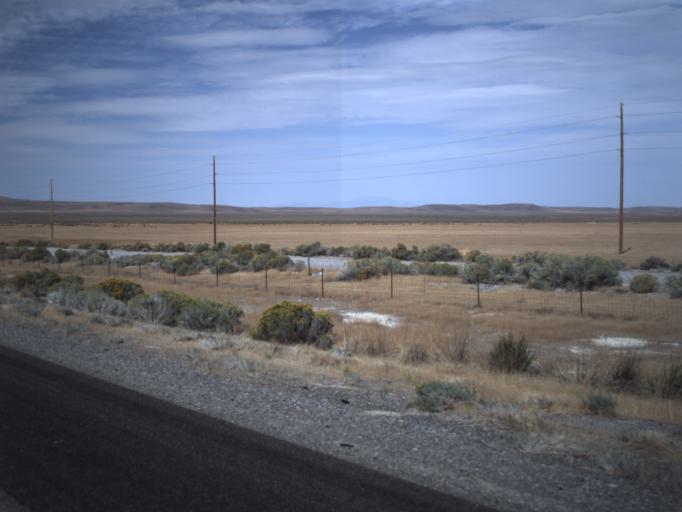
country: US
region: Utah
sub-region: Tooele County
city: Grantsville
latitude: 40.7538
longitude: -113.0363
